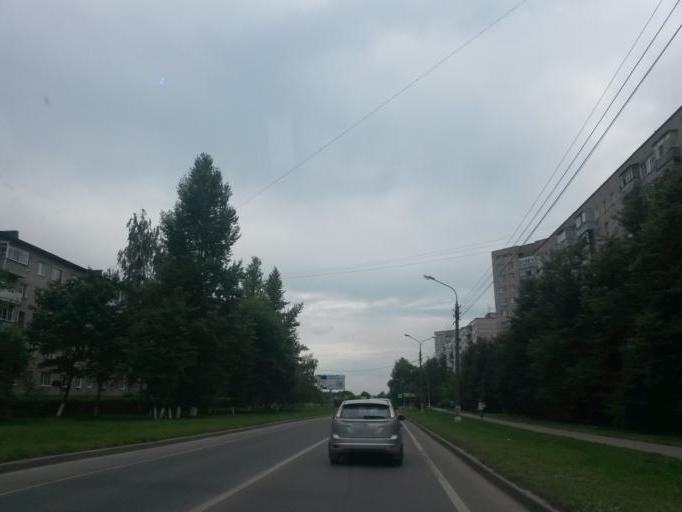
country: RU
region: Moskovskaya
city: Vostryakovo
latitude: 55.4140
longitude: 37.8330
